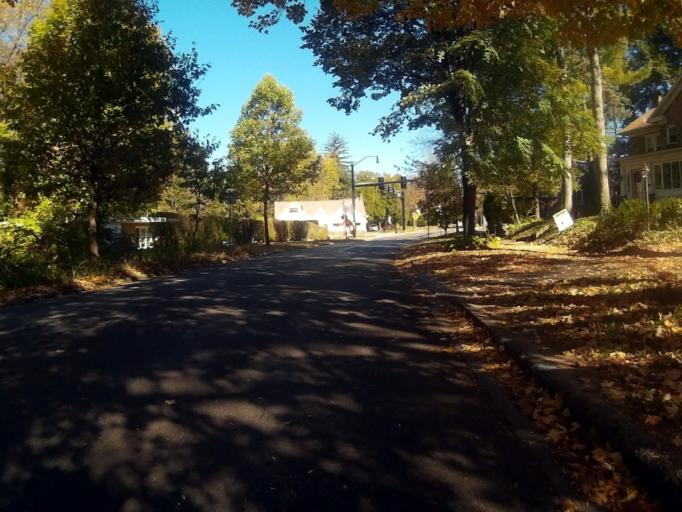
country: US
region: Pennsylvania
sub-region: Centre County
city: State College
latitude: 40.7982
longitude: -77.8760
